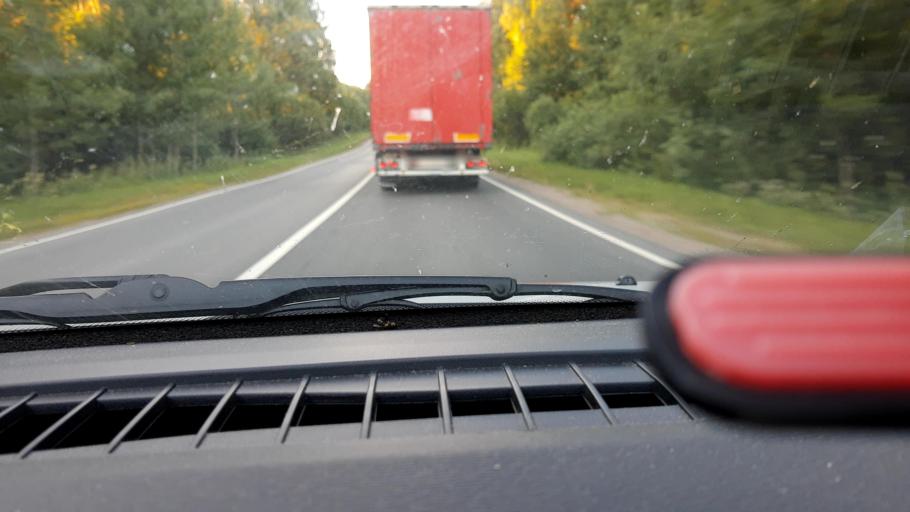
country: RU
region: Nizjnij Novgorod
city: Uren'
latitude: 57.2762
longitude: 45.6329
